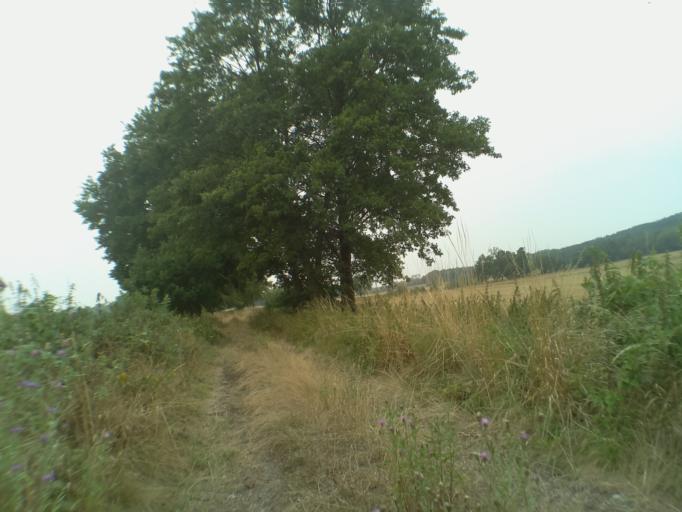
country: PL
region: Lower Silesian Voivodeship
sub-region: Powiat swidnicki
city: Strzegom
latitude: 50.9825
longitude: 16.3144
